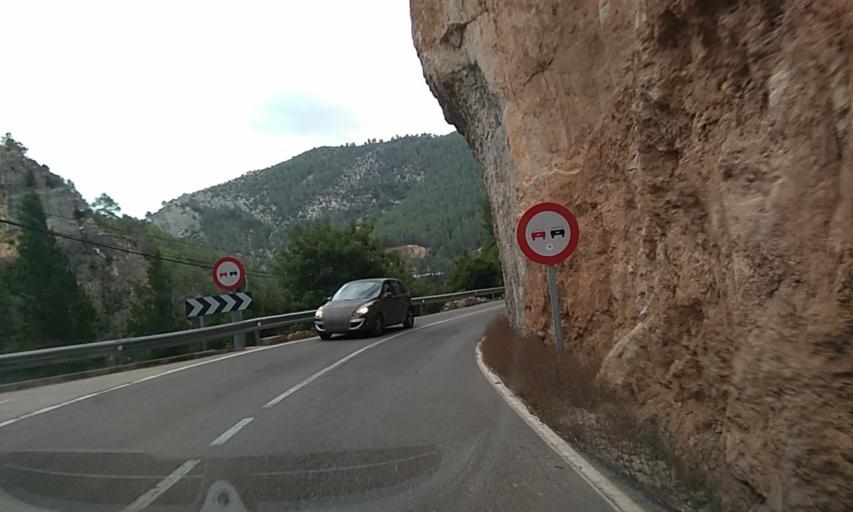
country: ES
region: Valencia
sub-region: Provincia de Castello
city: Montanejos
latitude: 40.0800
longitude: -0.5391
